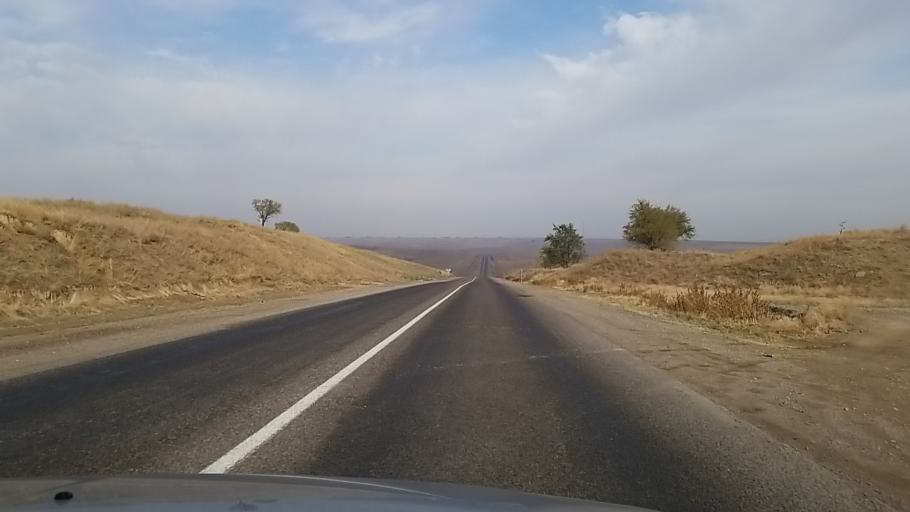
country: KZ
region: Almaty Oblysy
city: Burunday
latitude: 43.4869
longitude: 76.6708
